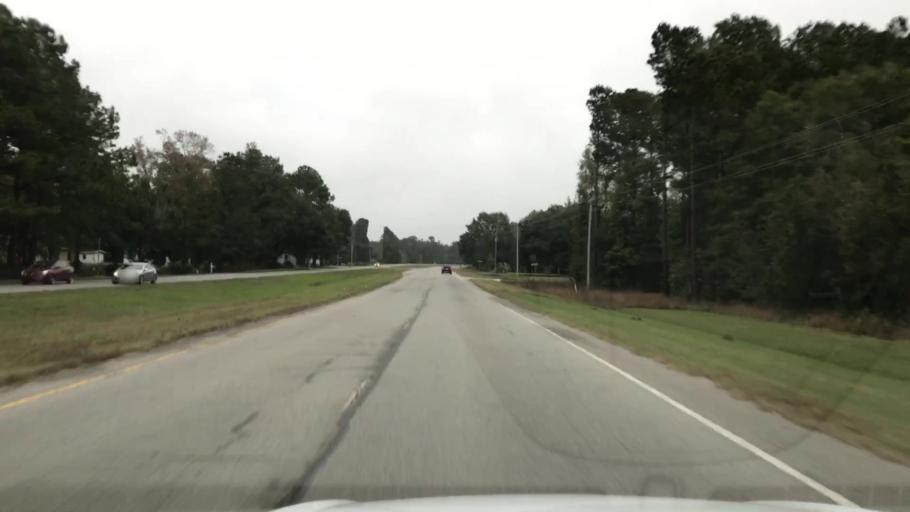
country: US
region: South Carolina
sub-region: Charleston County
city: Awendaw
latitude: 33.0412
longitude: -79.5903
